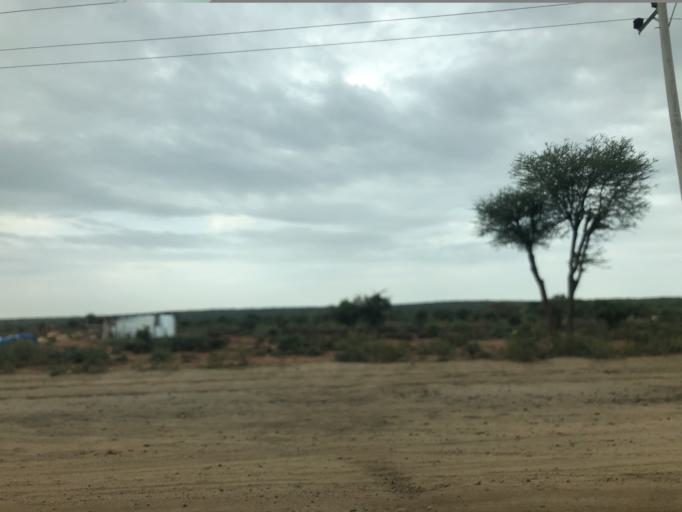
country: ET
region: Southern Nations, Nationalities, and People's Region
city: Turmi
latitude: 4.9920
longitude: 36.4732
